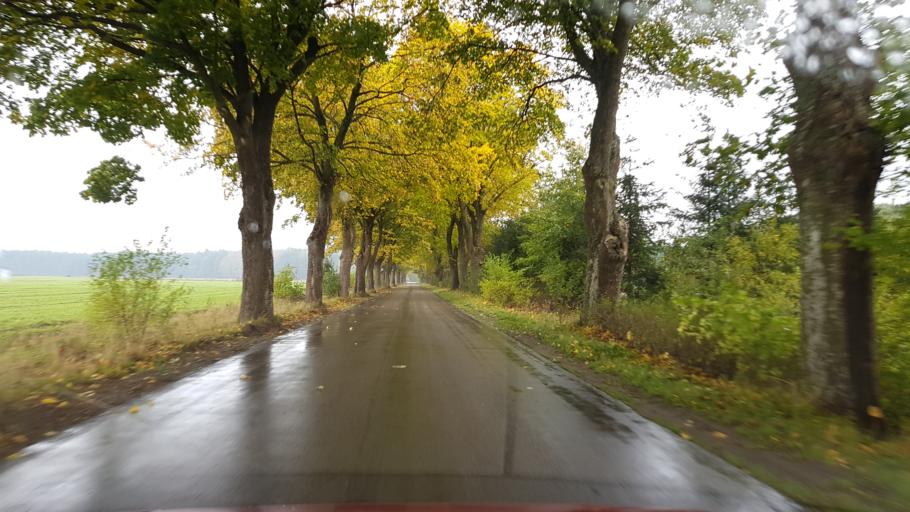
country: PL
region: West Pomeranian Voivodeship
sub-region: Powiat walecki
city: Walcz
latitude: 53.3524
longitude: 16.5628
